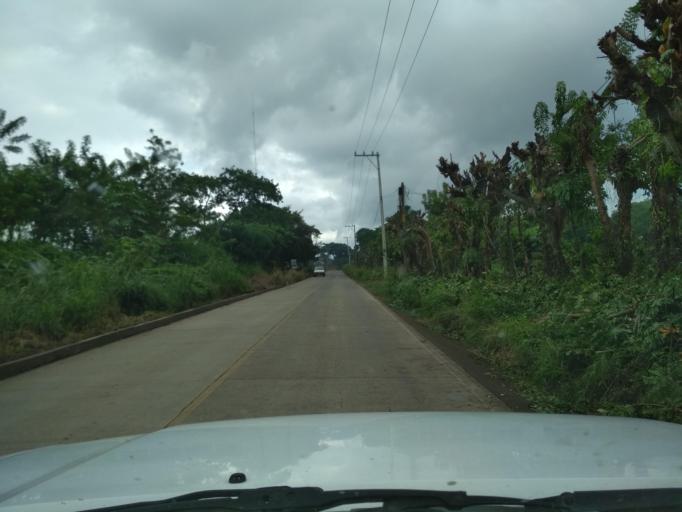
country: MX
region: Veracruz
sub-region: San Andres Tuxtla
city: Matacapan
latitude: 18.4231
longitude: -95.1771
